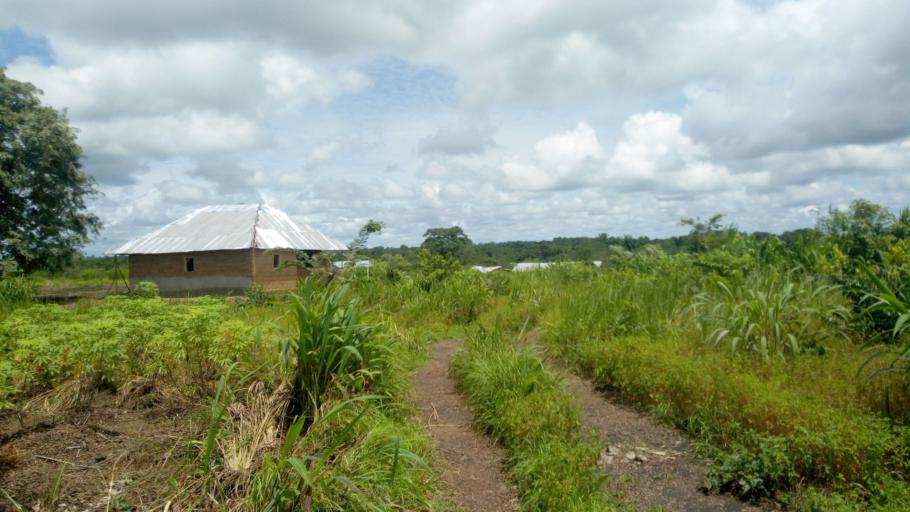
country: SL
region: Northern Province
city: Magburaka
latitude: 8.7109
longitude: -11.9542
